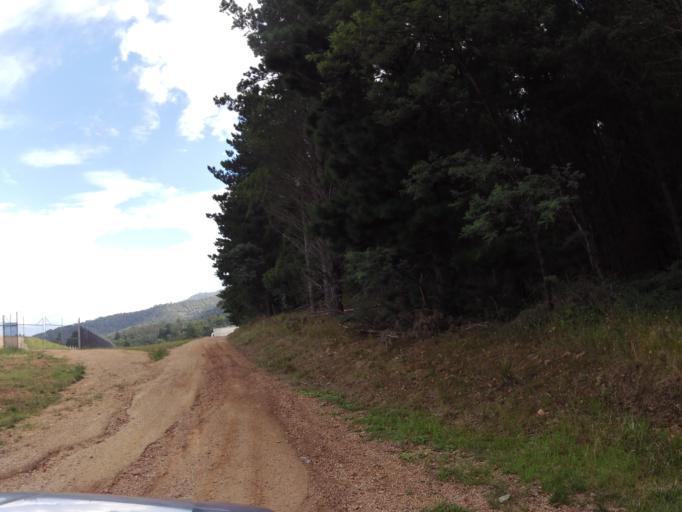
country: AU
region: Victoria
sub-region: Alpine
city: Mount Beauty
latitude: -36.7627
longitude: 147.0197
